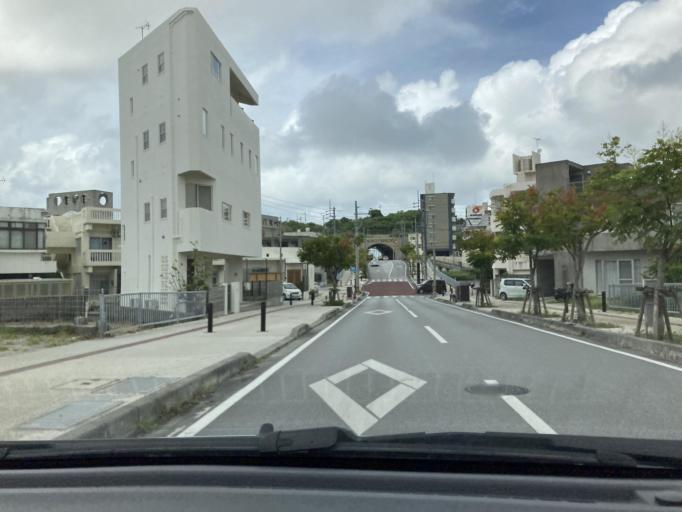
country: JP
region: Okinawa
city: Ginowan
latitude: 26.2350
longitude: 127.7345
